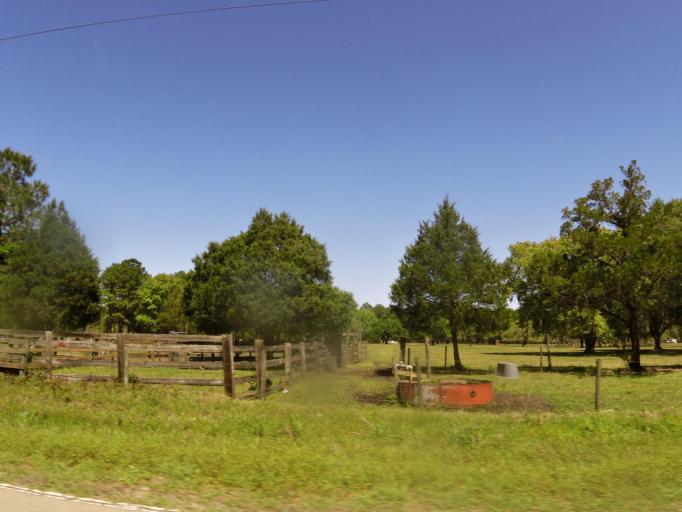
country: US
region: Florida
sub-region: Putnam County
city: East Palatka
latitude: 29.7747
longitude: -81.6085
